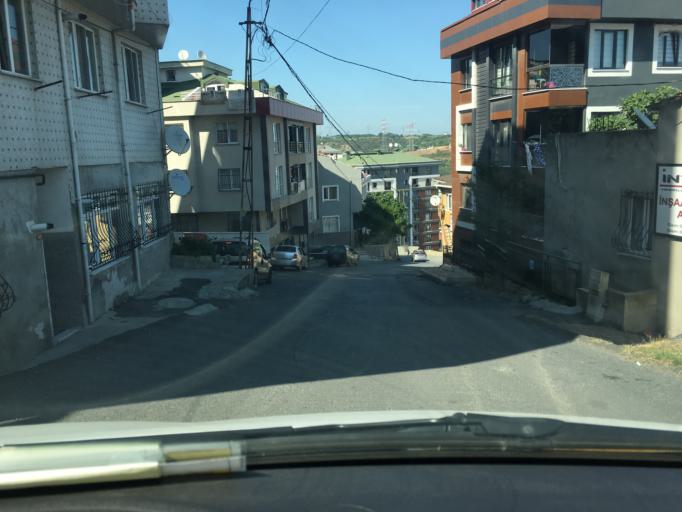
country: TR
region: Istanbul
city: Sisli
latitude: 41.0797
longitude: 28.9460
